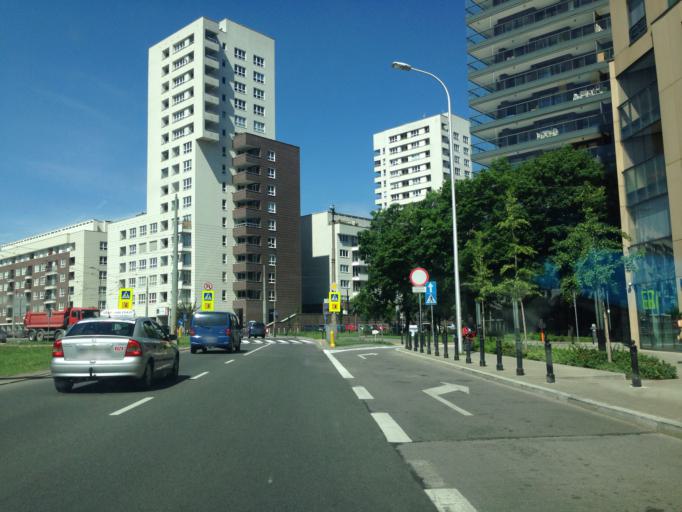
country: PL
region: Masovian Voivodeship
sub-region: Warszawa
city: Wola
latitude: 52.2540
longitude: 20.9946
